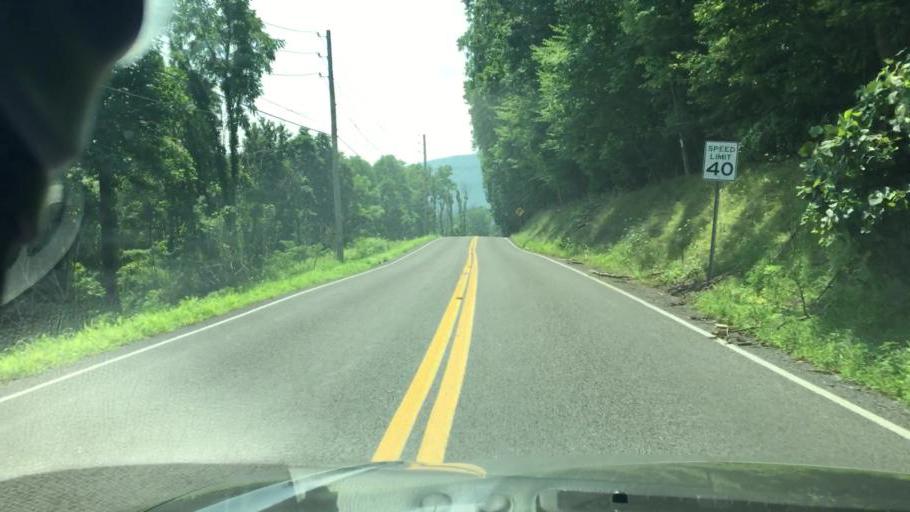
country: US
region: Pennsylvania
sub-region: Columbia County
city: Mifflinville
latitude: 41.0161
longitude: -76.3178
